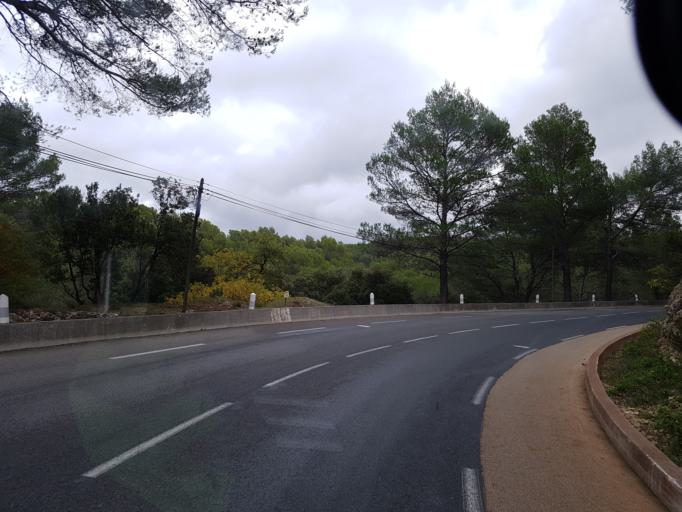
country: FR
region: Provence-Alpes-Cote d'Azur
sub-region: Departement des Bouches-du-Rhone
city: Cuges-les-Pins
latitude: 43.2686
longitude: 5.7358
